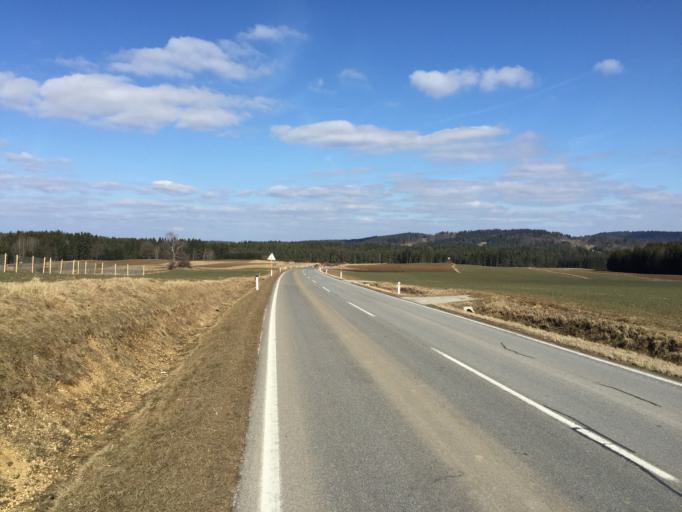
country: AT
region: Lower Austria
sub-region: Politischer Bezirk Gmund
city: Weitra
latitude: 48.6716
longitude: 14.9386
